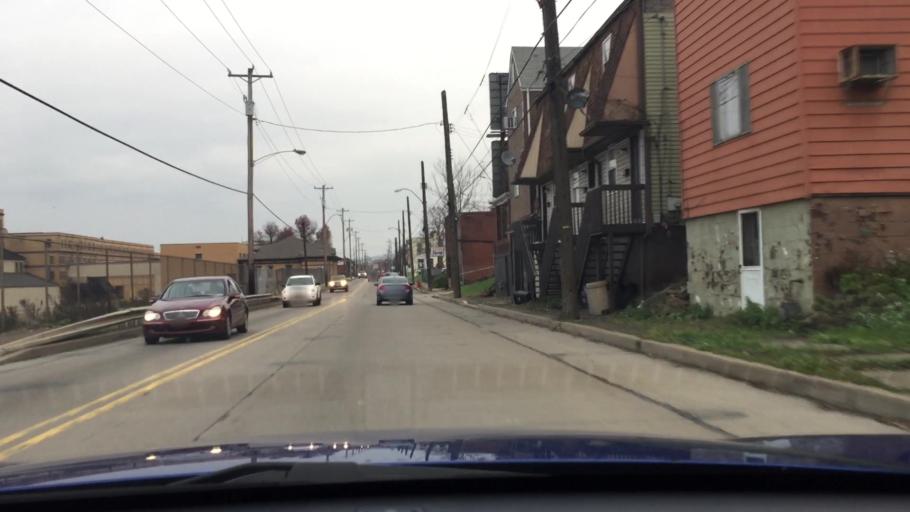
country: US
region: Pennsylvania
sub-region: Allegheny County
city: West Homestead
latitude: 40.3974
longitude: -79.9240
